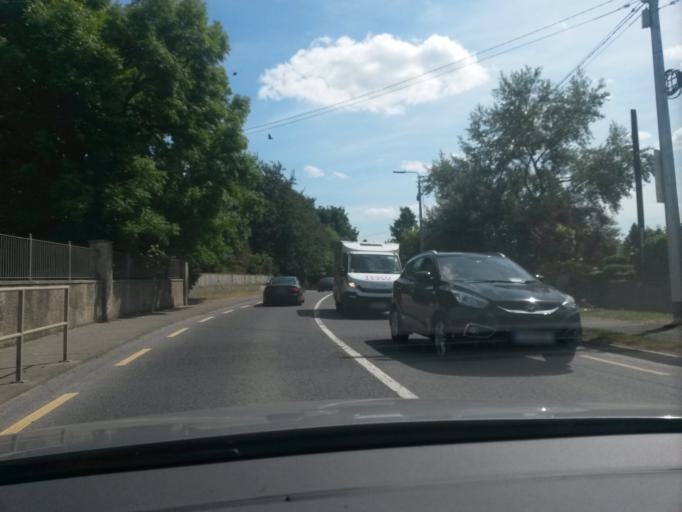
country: IE
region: Leinster
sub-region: Kildare
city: Sallins
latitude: 53.2557
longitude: -6.6675
